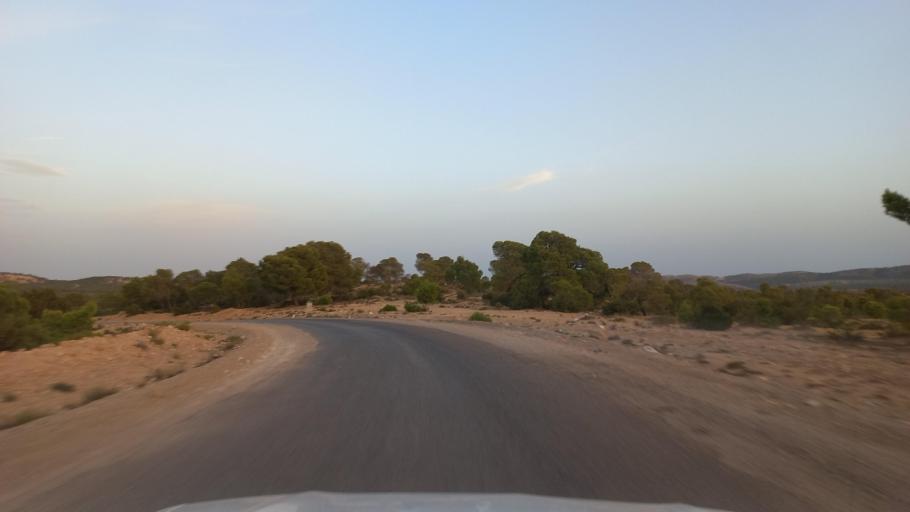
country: TN
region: Al Qasrayn
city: Sbiba
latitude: 35.4124
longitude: 8.9379
